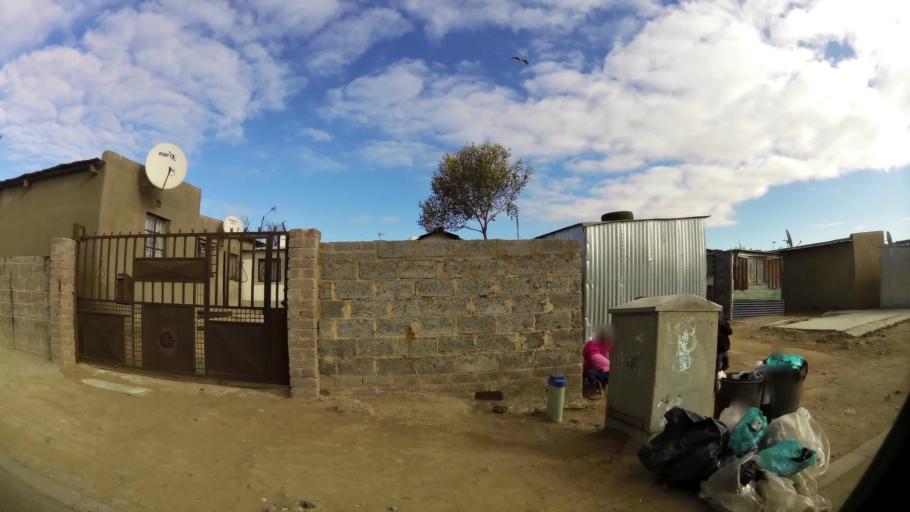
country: ZA
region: Gauteng
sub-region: Ekurhuleni Metropolitan Municipality
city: Tembisa
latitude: -26.0376
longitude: 28.1887
